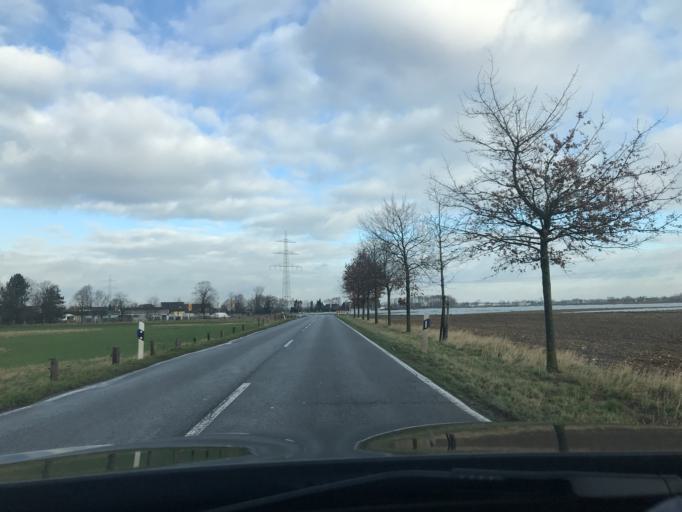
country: DE
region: North Rhine-Westphalia
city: Tonisvorst
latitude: 51.3467
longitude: 6.5017
